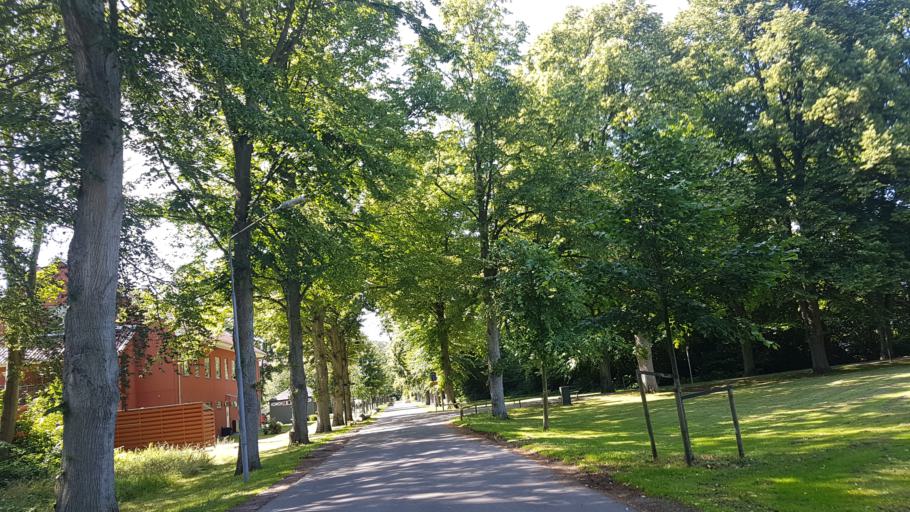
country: SE
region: Skane
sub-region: Helsingborg
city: Helsingborg
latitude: 56.0790
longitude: 12.6833
